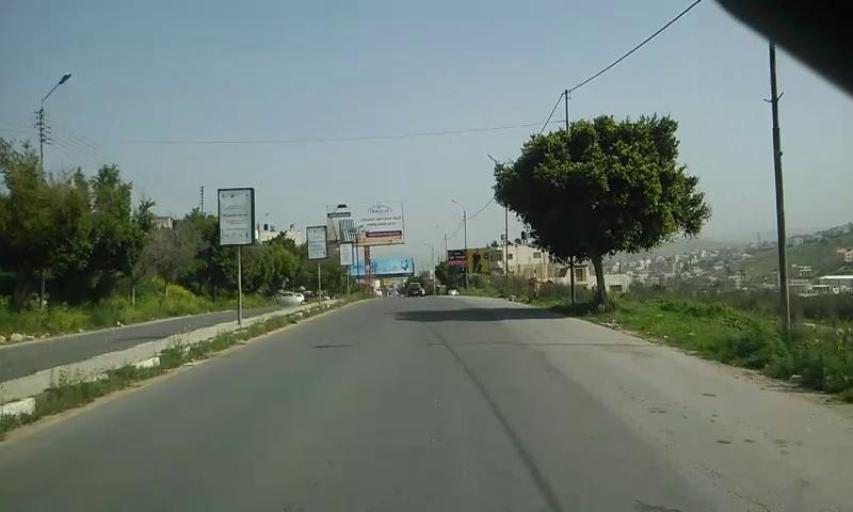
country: PS
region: West Bank
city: Kafr Qallil
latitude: 32.1855
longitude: 35.2793
